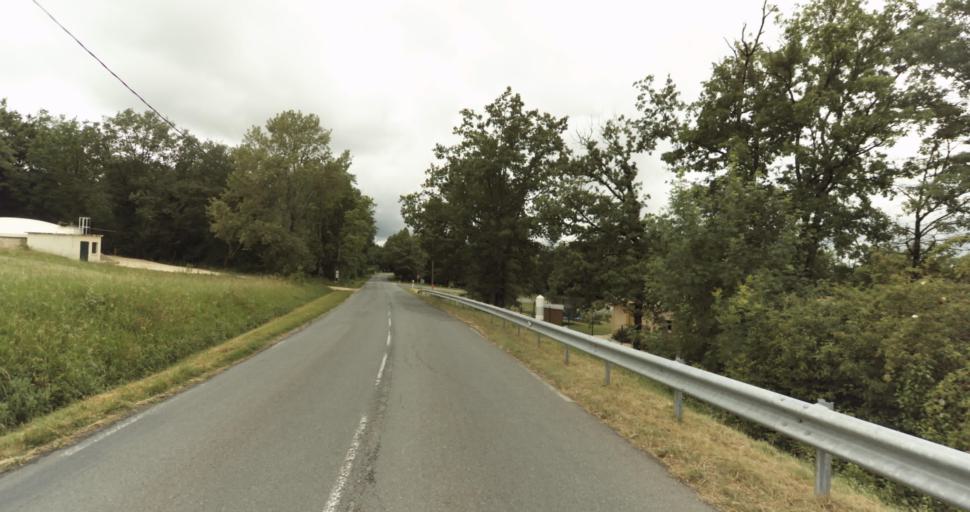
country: FR
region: Aquitaine
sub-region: Departement de la Dordogne
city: Beaumont-du-Perigord
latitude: 44.7482
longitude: 0.7786
